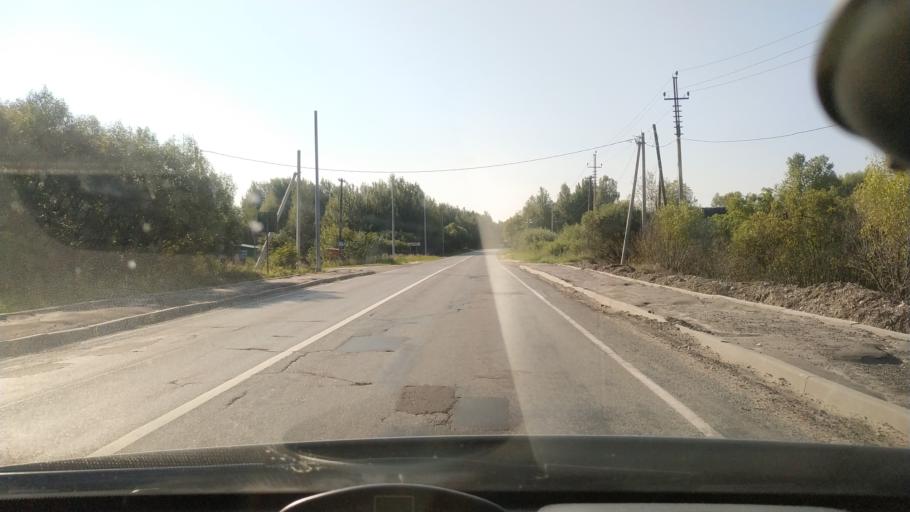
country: RU
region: Moskovskaya
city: Tugolesskiy Bor
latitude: 55.5345
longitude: 39.7080
